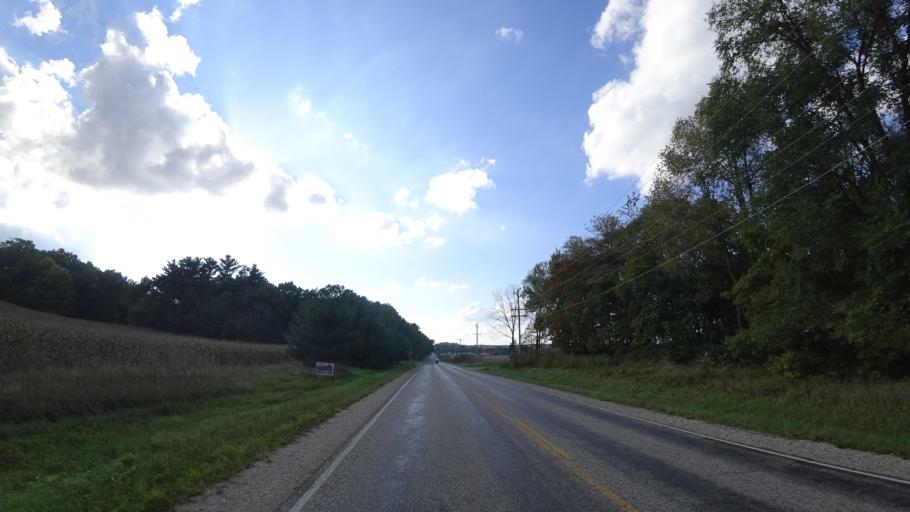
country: US
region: Michigan
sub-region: Saint Joseph County
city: Sturgis
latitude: 41.8538
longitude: -85.4568
